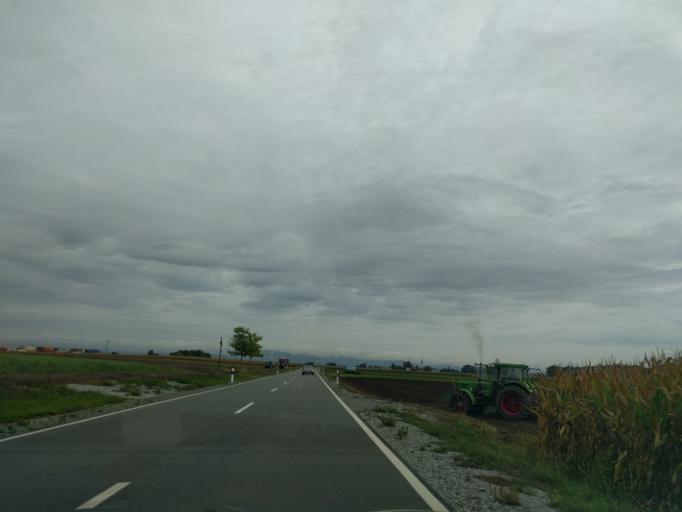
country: DE
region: Bavaria
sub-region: Lower Bavaria
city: Wallersdorf
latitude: 48.7439
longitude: 12.7647
